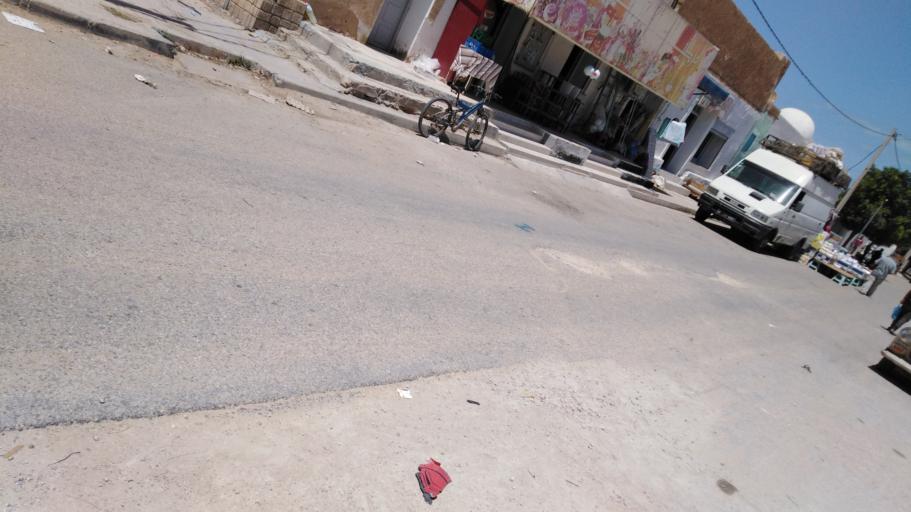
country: TN
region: Qabis
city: Matmata
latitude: 33.6171
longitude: 10.2898
